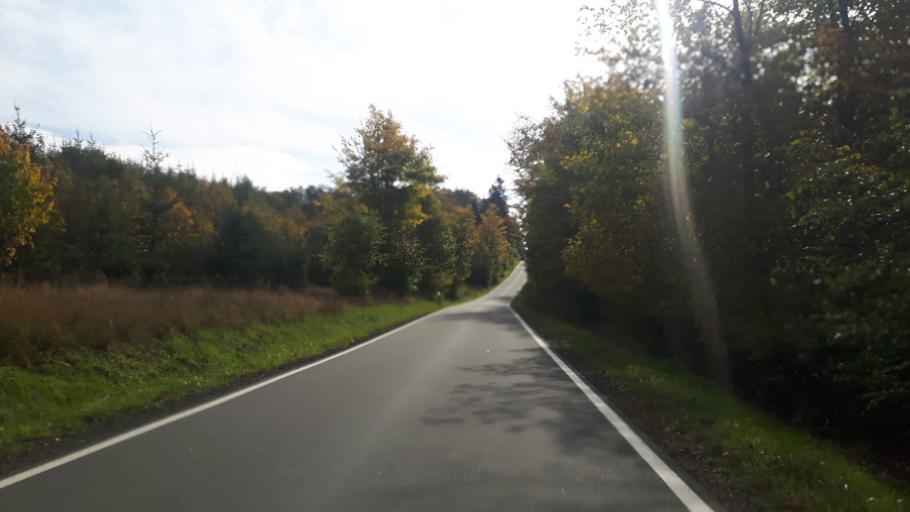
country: DE
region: North Rhine-Westphalia
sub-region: Regierungsbezirk Arnsberg
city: Erndtebruck
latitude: 50.9160
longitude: 8.2458
